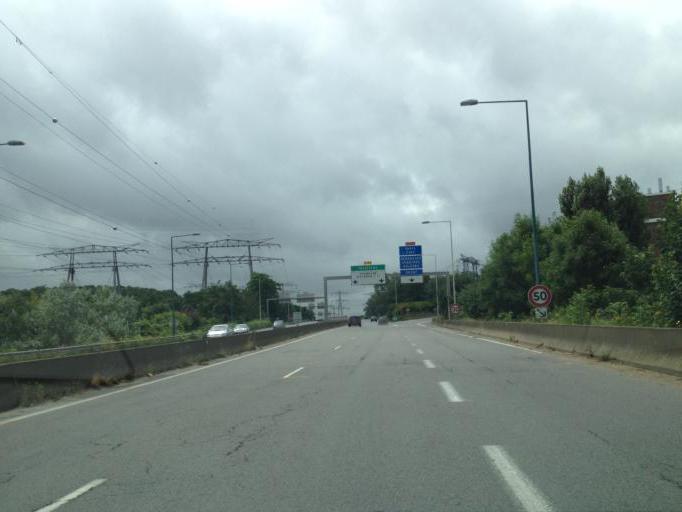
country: FR
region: Ile-de-France
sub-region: Departement de l'Essonne
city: Champlan
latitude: 48.7189
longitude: 2.2699
